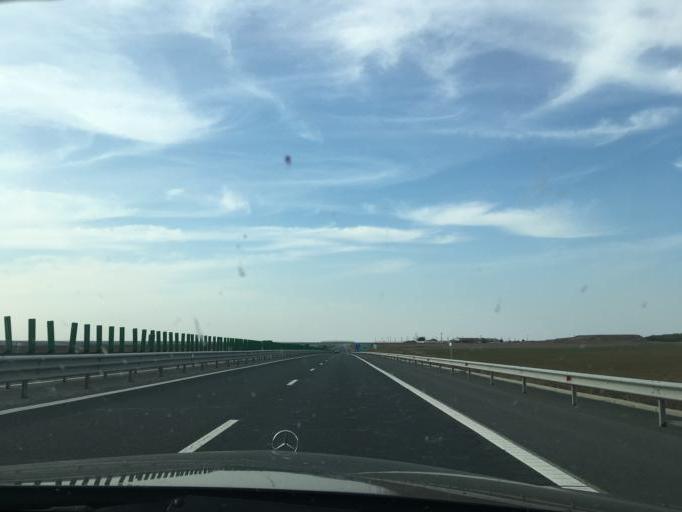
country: RO
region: Constanta
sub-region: Municipiul Medgidia
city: Valea Dacilor
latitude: 44.1810
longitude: 28.3133
